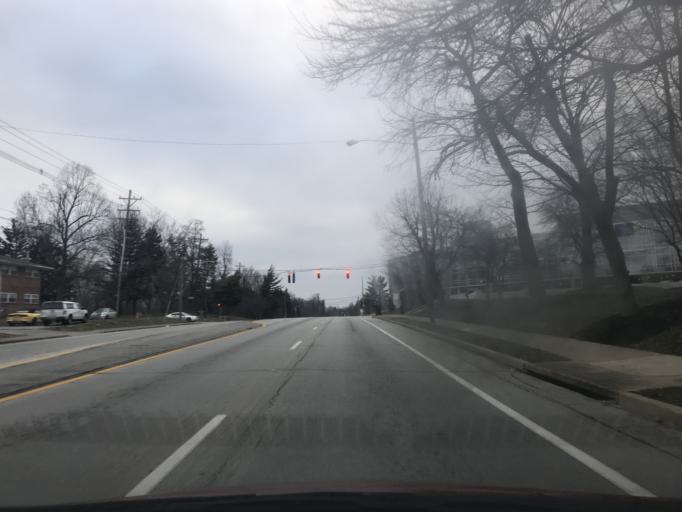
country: US
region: Kentucky
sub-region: Jefferson County
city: Audubon Park
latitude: 38.2135
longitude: -85.7224
